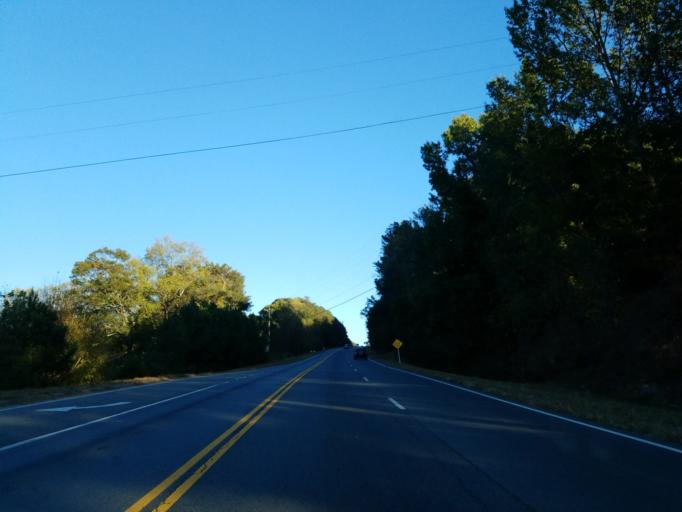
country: US
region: Georgia
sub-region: Dawson County
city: Dawsonville
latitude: 34.3809
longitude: -84.0599
